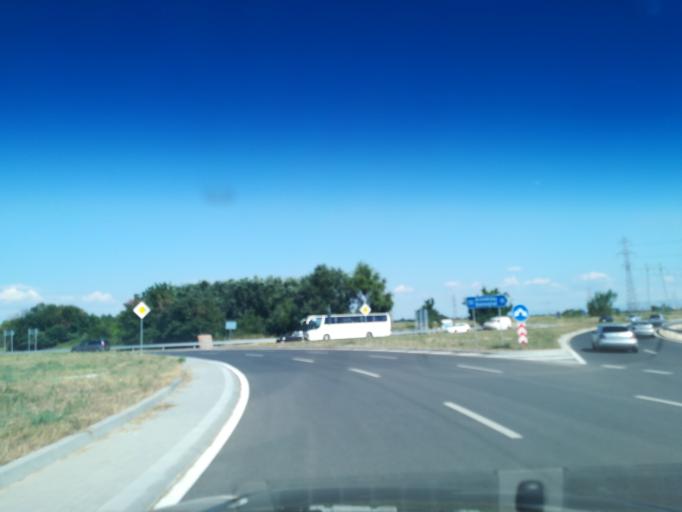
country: BG
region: Plovdiv
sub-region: Obshtina Plovdiv
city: Plovdiv
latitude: 42.0985
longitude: 24.7881
